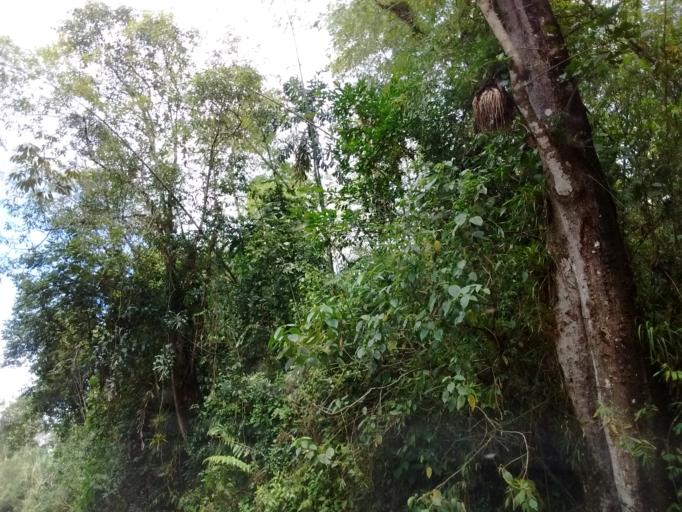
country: CO
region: Cauca
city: Morales
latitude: 2.6847
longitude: -76.7612
